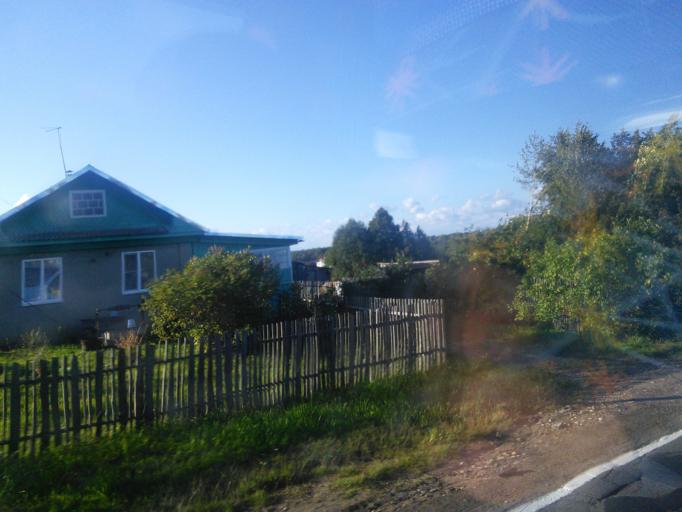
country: RU
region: Jaroslavl
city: Poshekhon'ye
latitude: 58.4253
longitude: 38.9960
